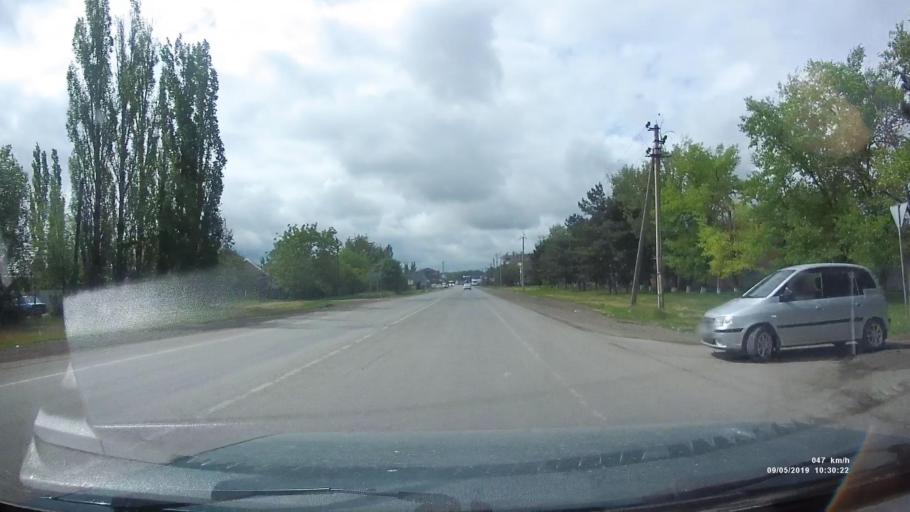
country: RU
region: Rostov
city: Azov
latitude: 47.0904
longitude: 39.4305
